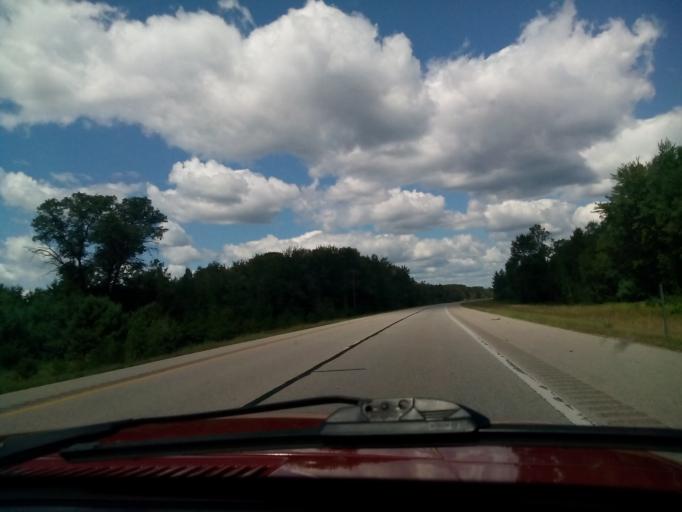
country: US
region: Michigan
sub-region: Ogemaw County
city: Skidway Lake
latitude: 44.1046
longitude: -84.1149
